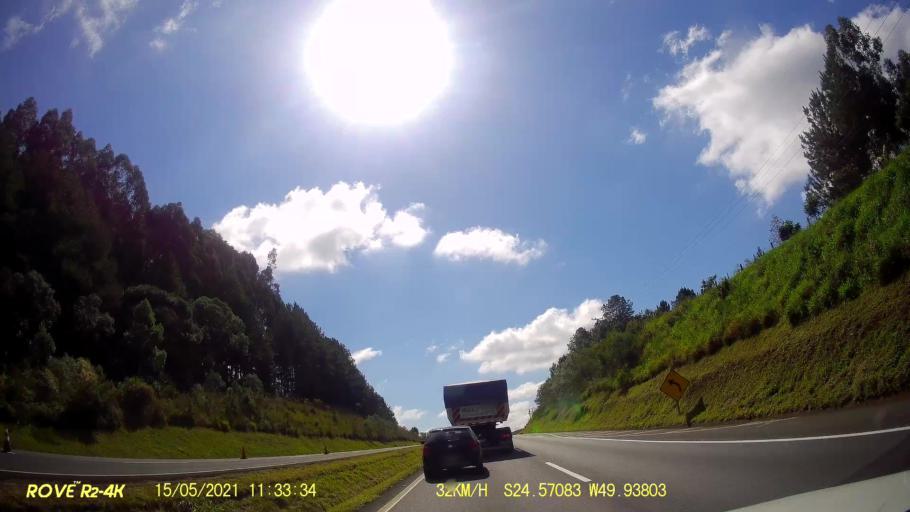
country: BR
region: Parana
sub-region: Pirai Do Sul
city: Pirai do Sul
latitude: -24.5709
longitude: -49.9381
